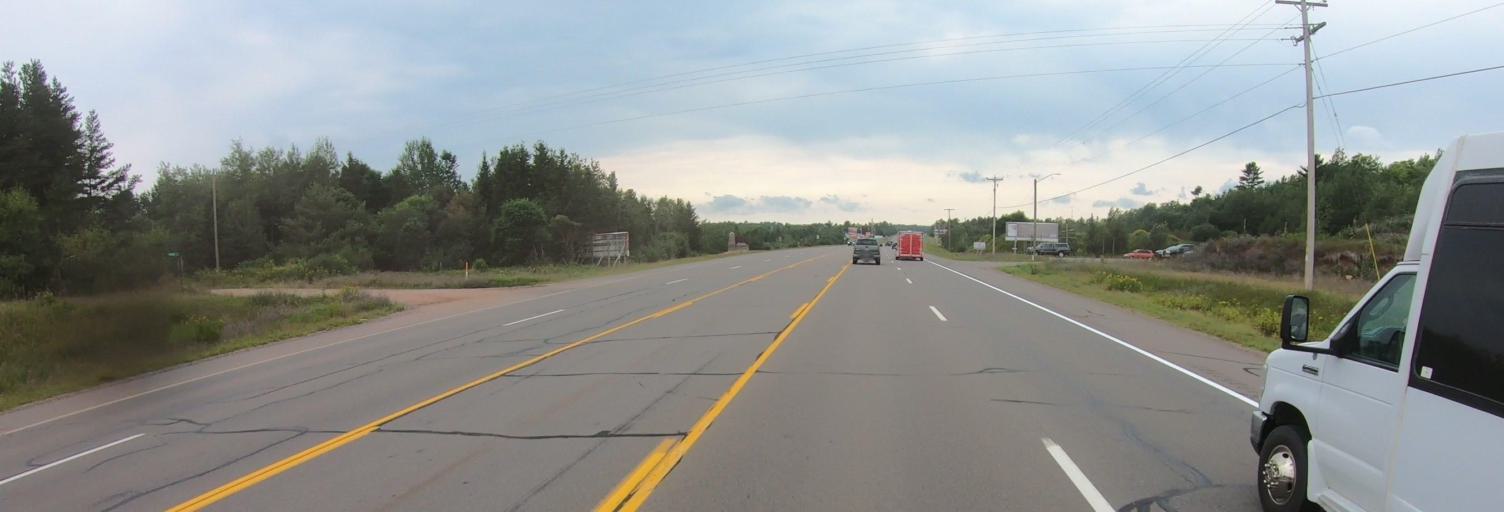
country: US
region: Michigan
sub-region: Marquette County
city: West Ishpeming
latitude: 46.4952
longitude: -87.6920
